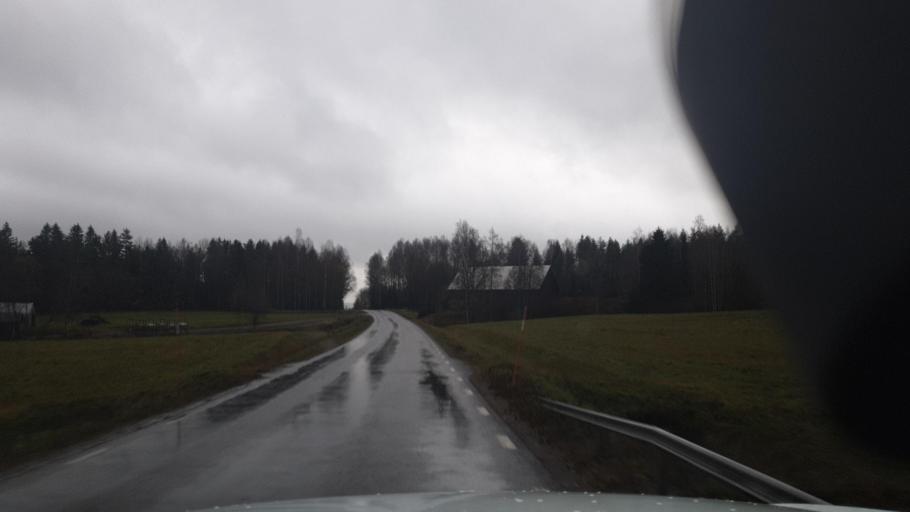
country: SE
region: Vaermland
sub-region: Eda Kommun
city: Charlottenberg
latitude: 59.7922
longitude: 12.1543
